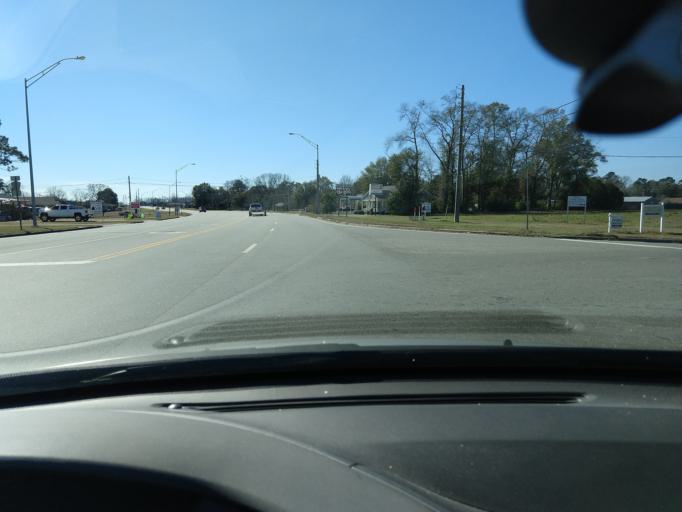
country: US
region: Alabama
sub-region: Covington County
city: Andalusia
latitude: 31.2927
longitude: -86.5022
